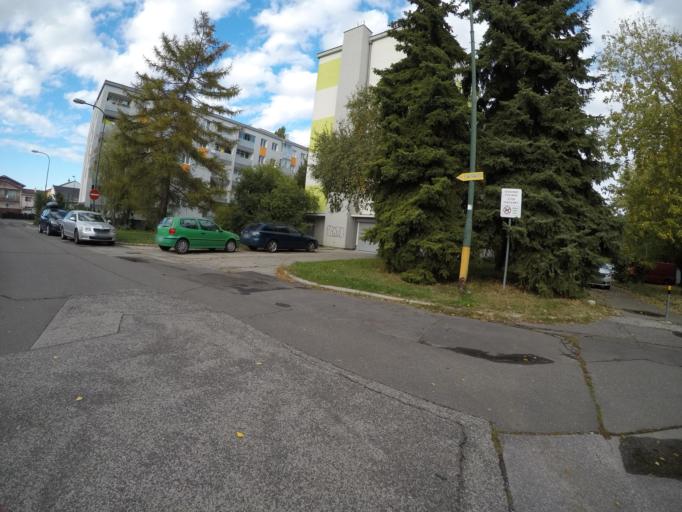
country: SK
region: Bratislavsky
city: Bratislava
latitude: 48.1664
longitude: 17.1709
